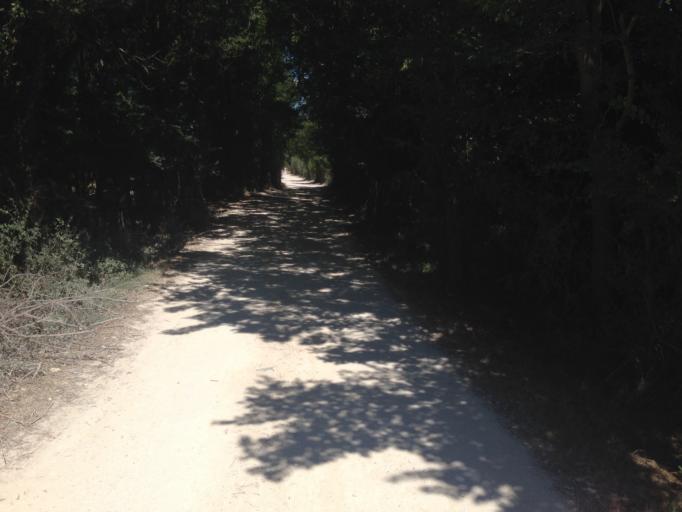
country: HR
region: Istarska
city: Medulin
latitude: 44.7884
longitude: 13.9104
